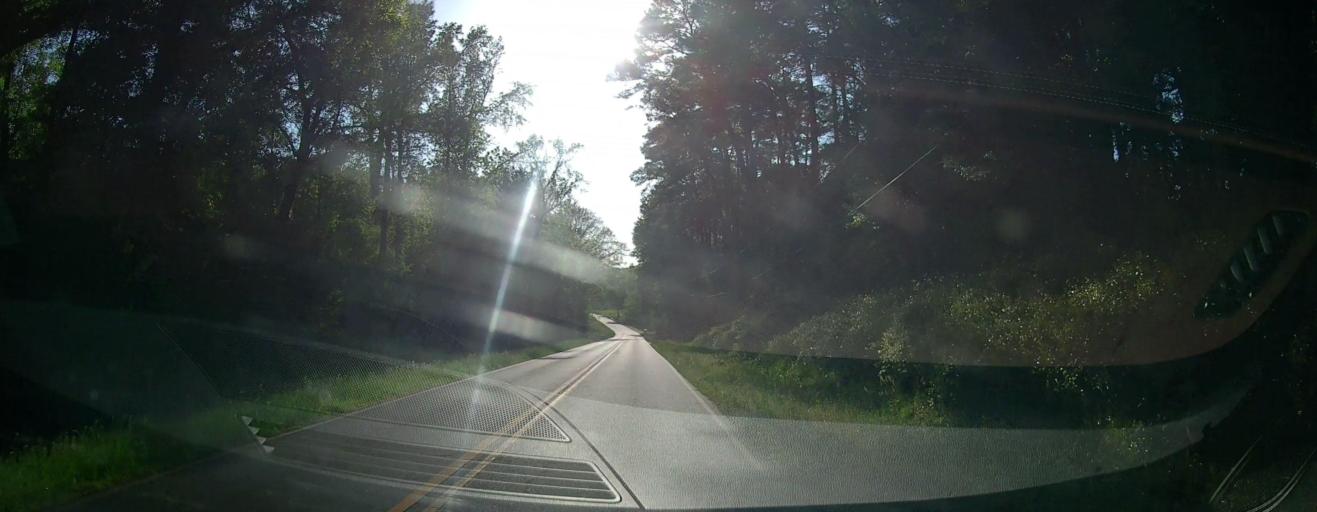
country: US
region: Georgia
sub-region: Macon County
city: Montezuma
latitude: 32.3141
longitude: -84.0059
